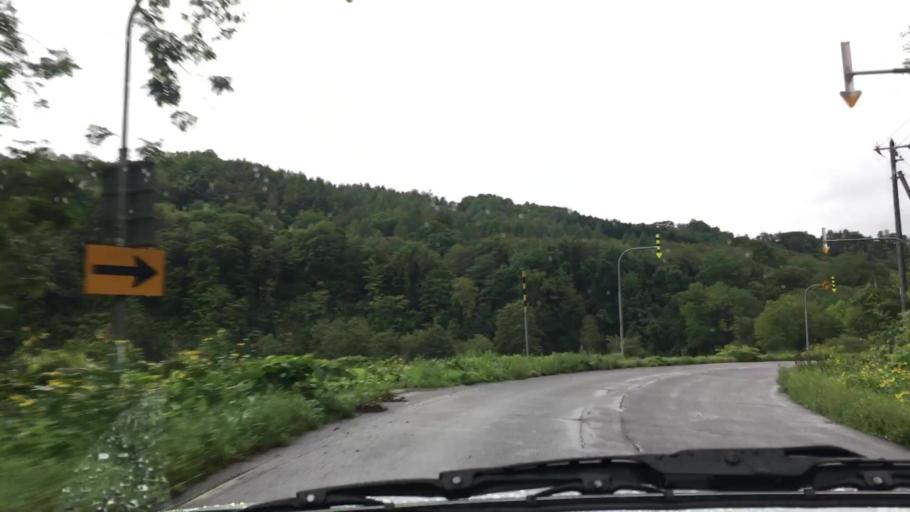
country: JP
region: Hokkaido
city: Niseko Town
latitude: 42.6634
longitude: 140.7771
